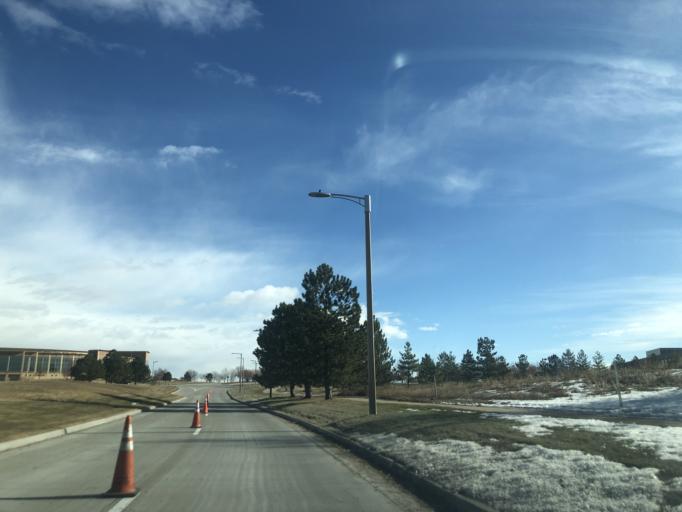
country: US
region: Colorado
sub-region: Douglas County
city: Meridian
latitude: 39.5480
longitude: -104.8472
